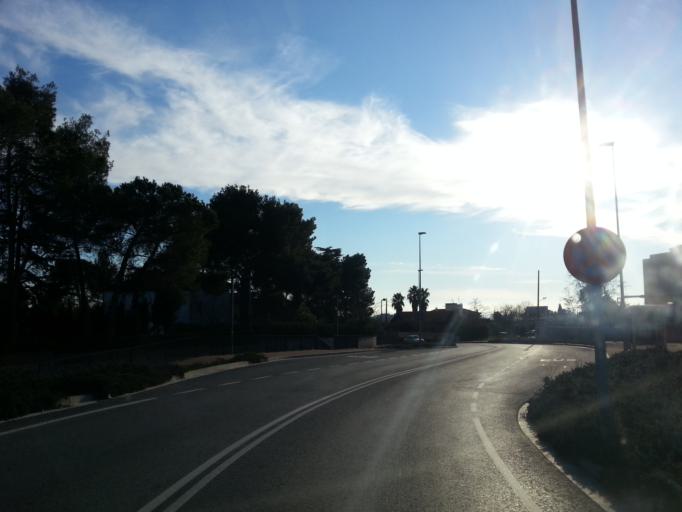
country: ES
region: Catalonia
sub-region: Provincia de Barcelona
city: Matadepera
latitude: 41.5911
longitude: 2.0198
